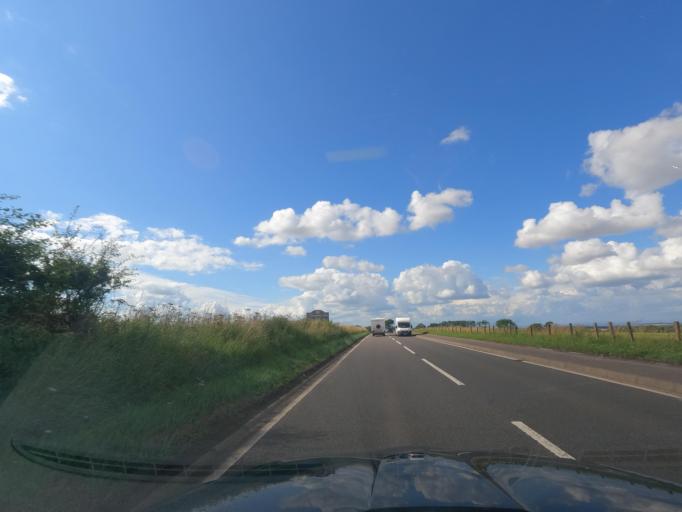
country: GB
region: Scotland
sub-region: East Lothian
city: Pencaitland
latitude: 55.8296
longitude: -2.8837
